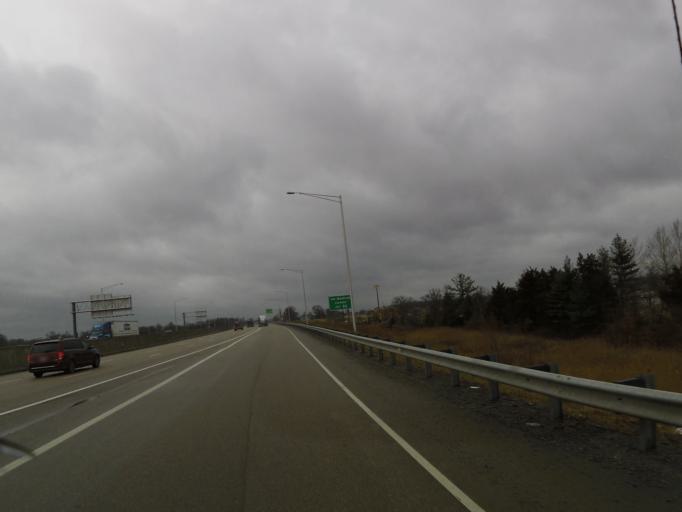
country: US
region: Illinois
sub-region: Williamson County
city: Marion
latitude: 37.7367
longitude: -88.9591
